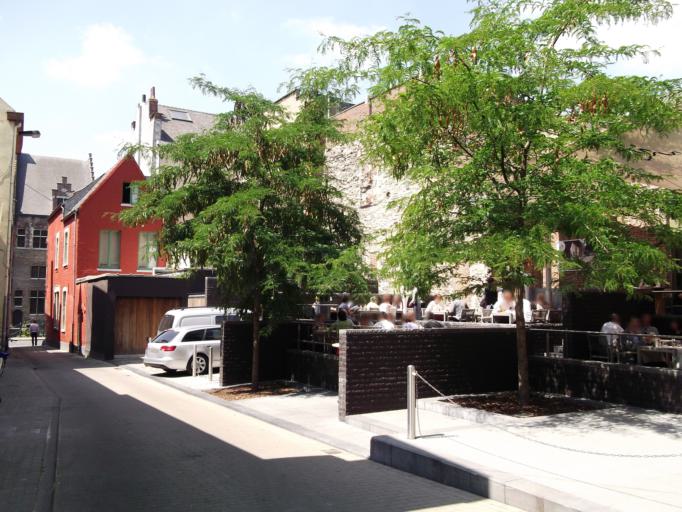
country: BE
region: Flanders
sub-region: Provincie Oost-Vlaanderen
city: Gent
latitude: 51.0525
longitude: 3.7216
